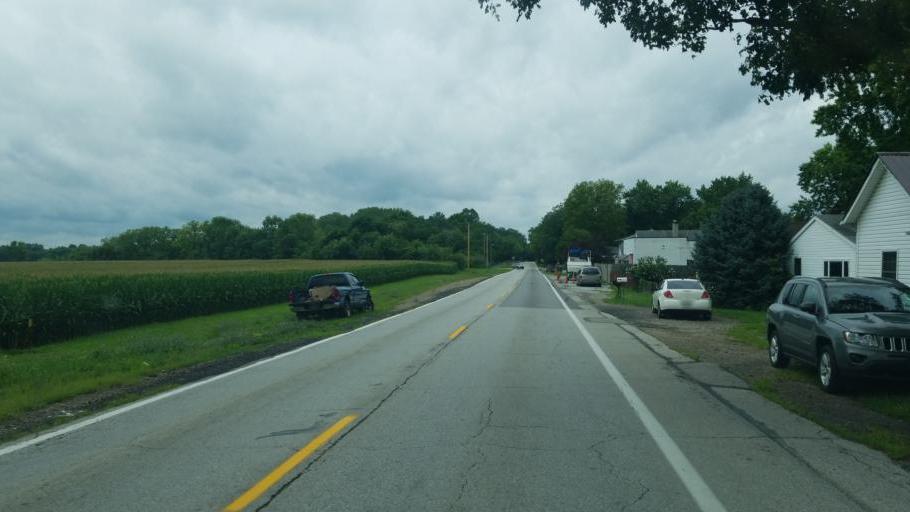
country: US
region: Ohio
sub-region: Franklin County
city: Obetz
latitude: 39.8322
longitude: -83.0040
